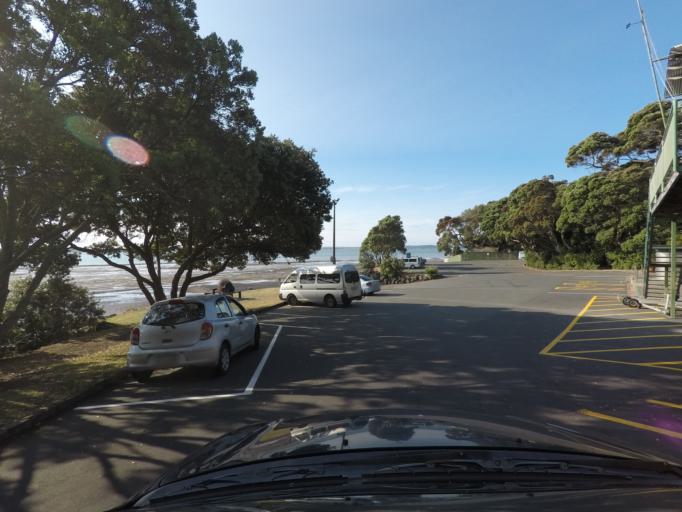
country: NZ
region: Auckland
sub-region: Auckland
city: Rosebank
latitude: -36.8603
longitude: 174.6994
